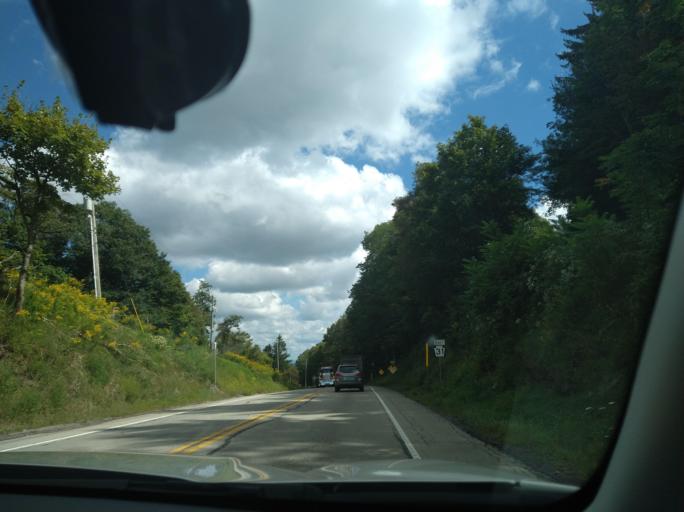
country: US
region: Pennsylvania
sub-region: Westmoreland County
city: Ligonier
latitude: 40.0672
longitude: -79.2666
